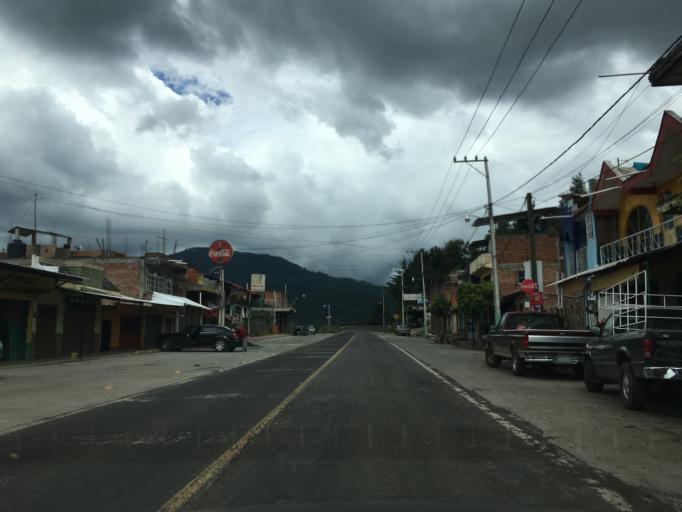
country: MX
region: Michoacan
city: Cheran
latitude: 19.6883
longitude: -101.9588
